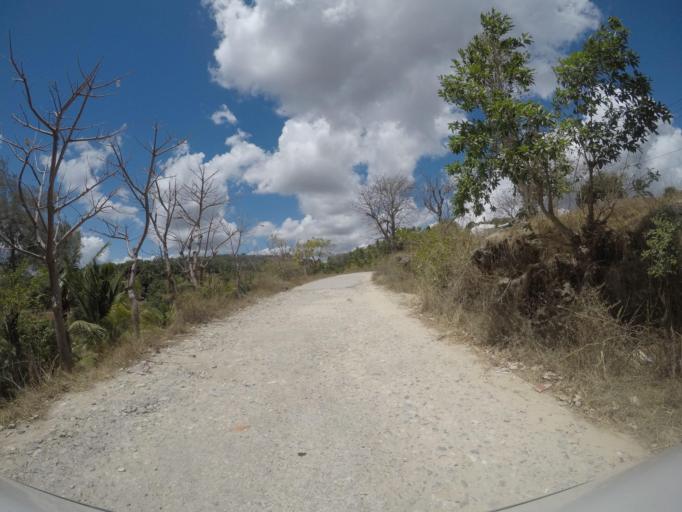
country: TL
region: Baucau
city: Baucau
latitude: -8.4826
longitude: 126.6323
